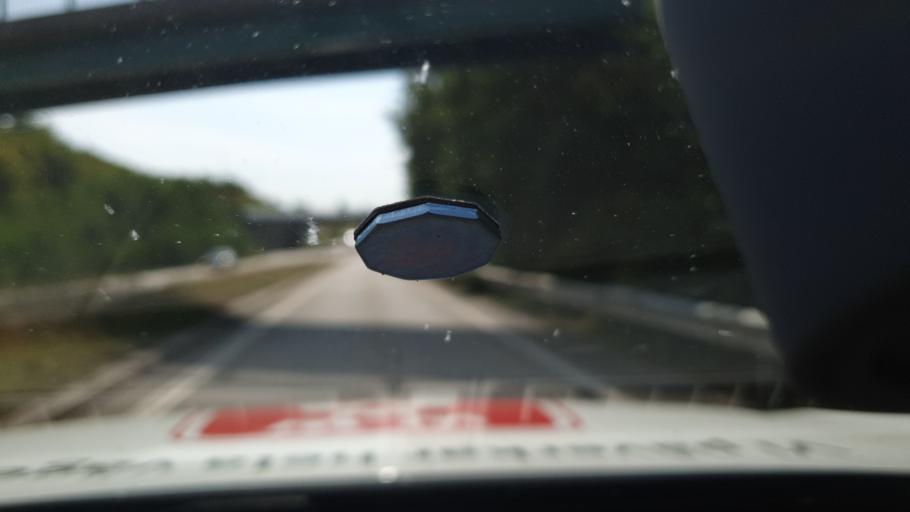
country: SE
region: Skane
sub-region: Burlovs Kommun
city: Arloev
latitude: 55.6373
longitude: 13.0927
